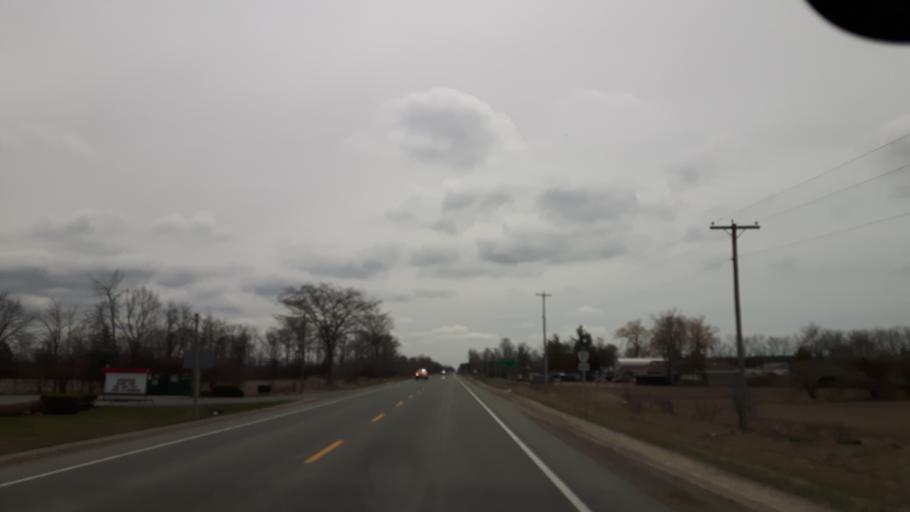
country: CA
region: Ontario
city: Goderich
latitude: 43.7215
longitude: -81.7058
